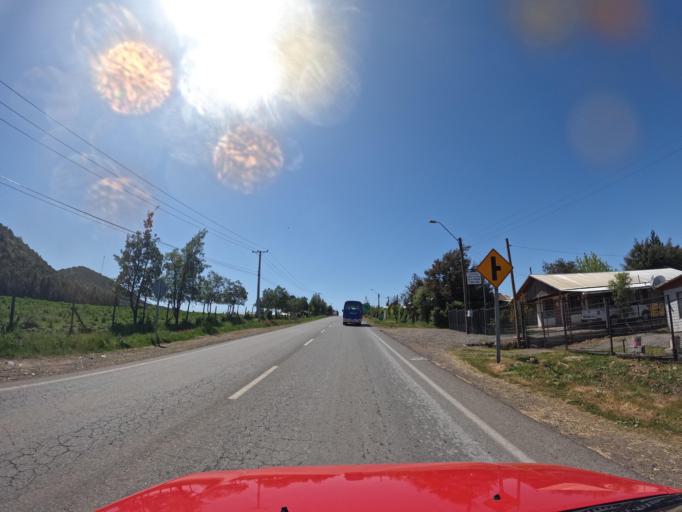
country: CL
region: Maule
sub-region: Provincia de Talca
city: San Clemente
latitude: -35.5651
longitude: -71.3595
